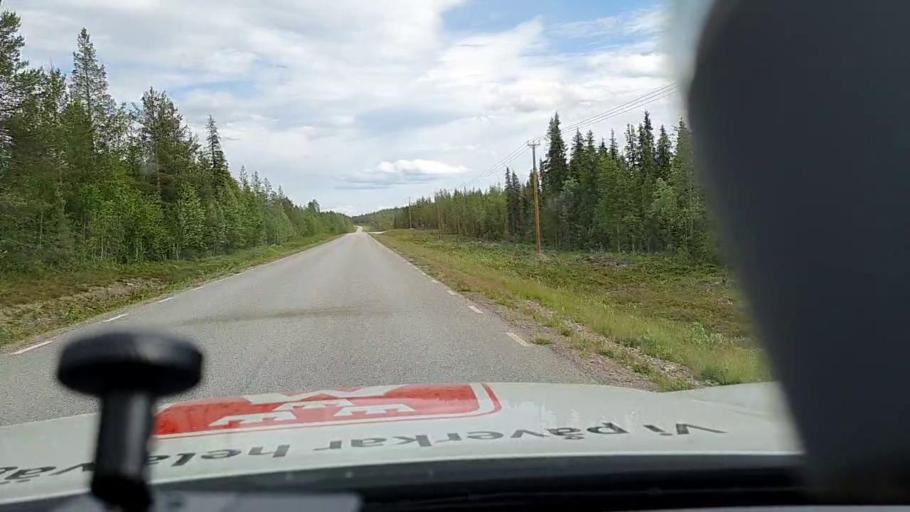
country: SE
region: Norrbotten
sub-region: Jokkmokks Kommun
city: Jokkmokk
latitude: 66.6568
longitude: 19.9724
